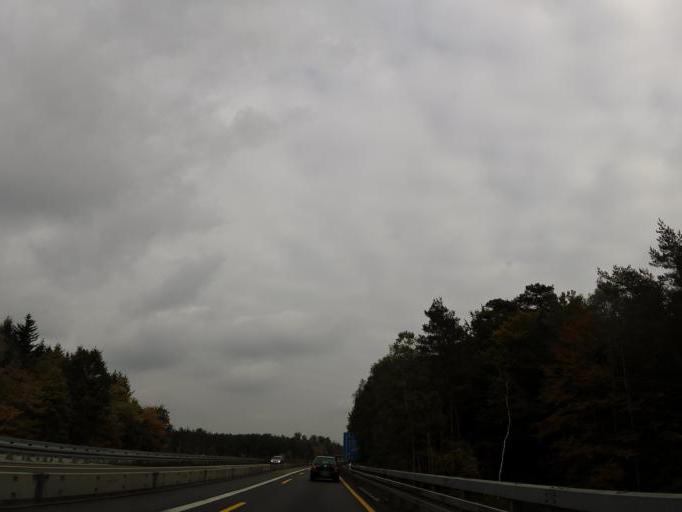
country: DE
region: Rheinland-Pfalz
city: Waldmohr
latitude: 49.3692
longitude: 7.3575
